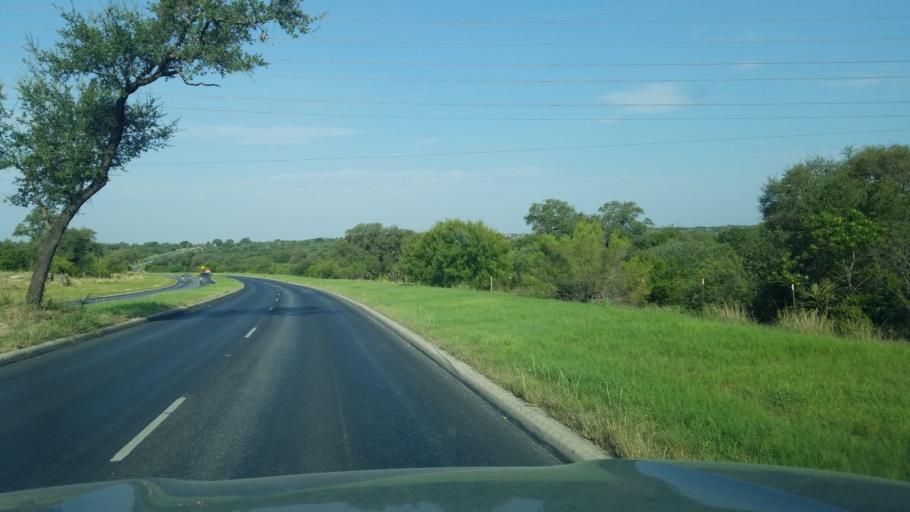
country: US
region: Texas
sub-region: Bexar County
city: Leon Valley
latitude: 29.4655
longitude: -98.7184
